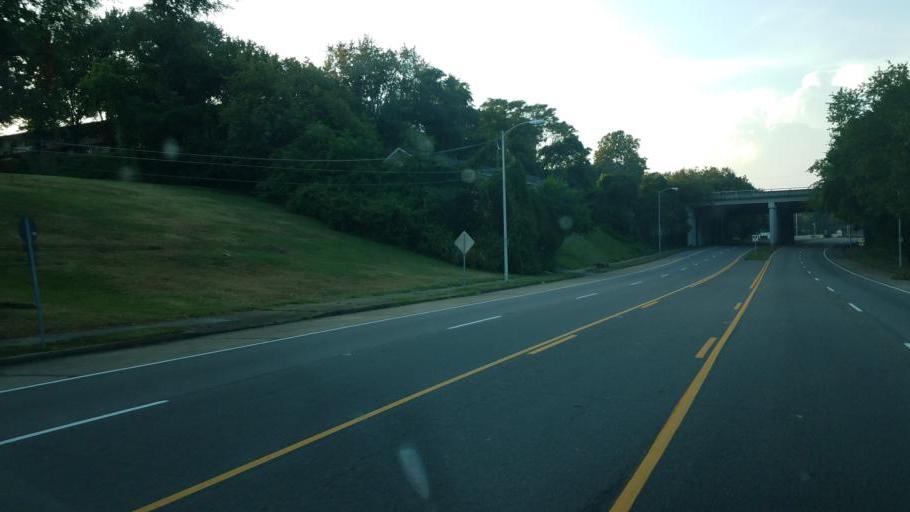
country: US
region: Tennessee
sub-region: Sullivan County
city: Kingsport
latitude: 36.5578
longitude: -82.5677
